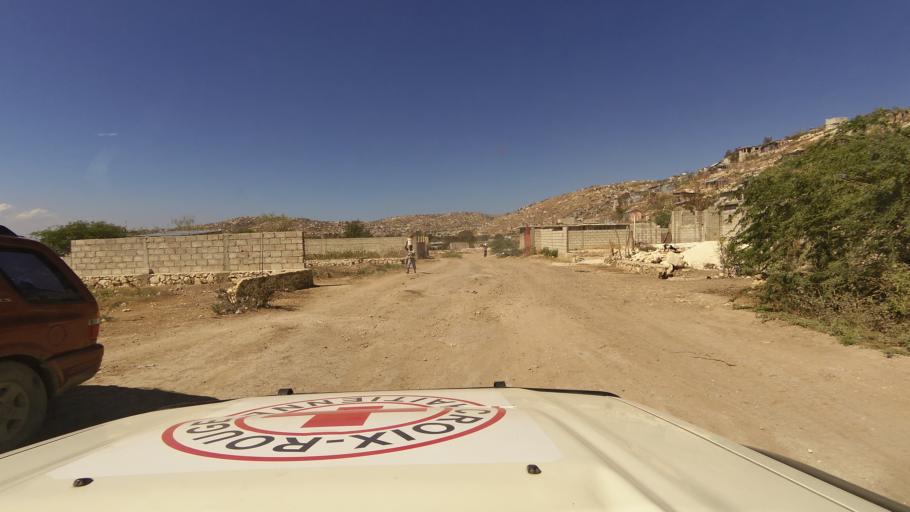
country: HT
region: Ouest
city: Croix des Bouquets
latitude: 18.6615
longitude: -72.2558
